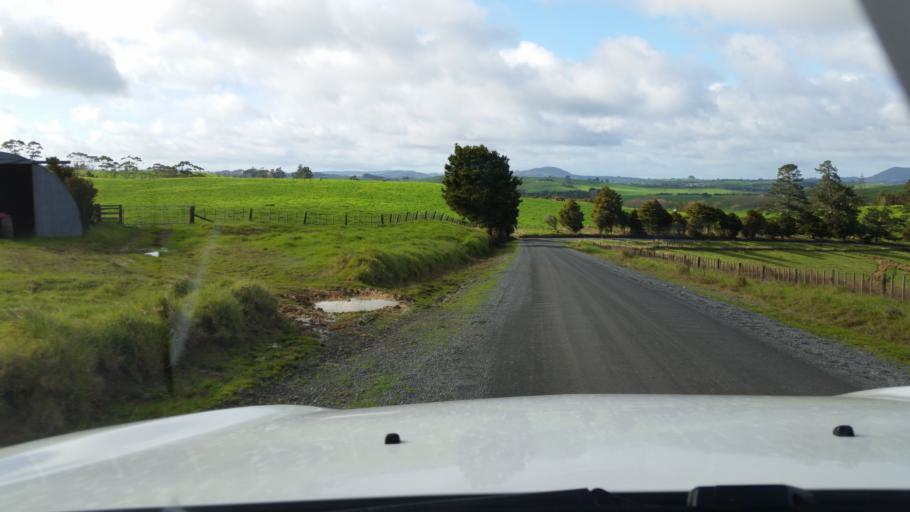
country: NZ
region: Northland
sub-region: Whangarei
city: Maungatapere
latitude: -35.6720
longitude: 174.1008
